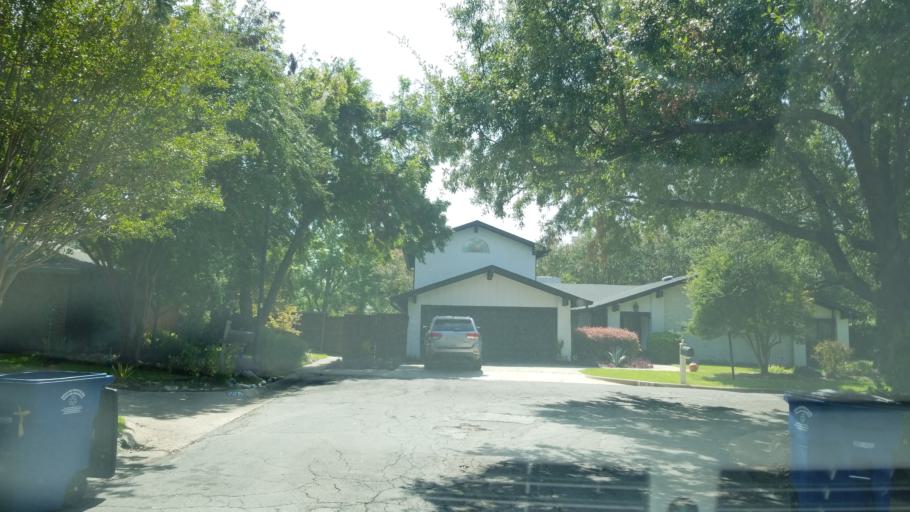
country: US
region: Texas
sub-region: Dallas County
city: Addison
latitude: 32.9641
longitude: -96.7821
